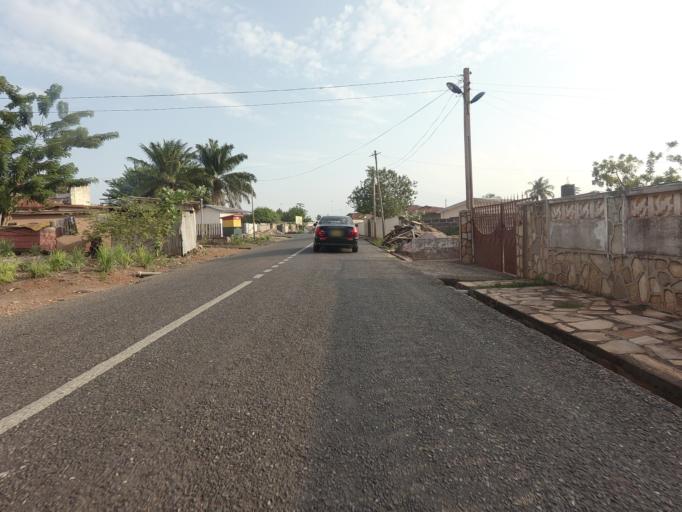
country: GH
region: Volta
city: Ho
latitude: 6.6058
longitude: 0.4705
